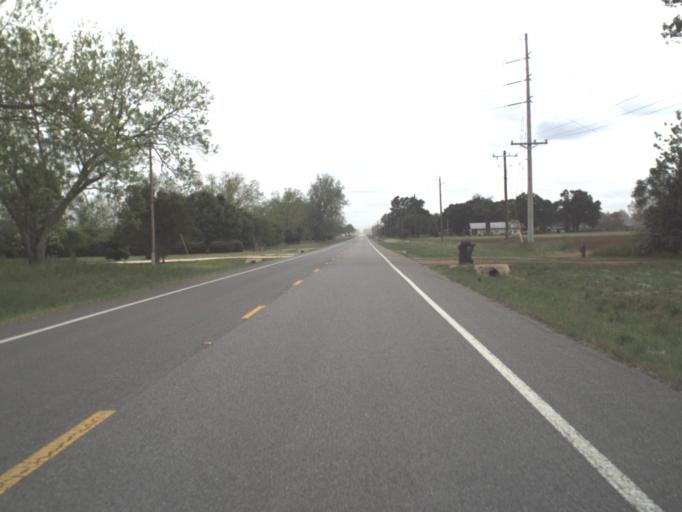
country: US
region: Florida
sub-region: Santa Rosa County
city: Point Baker
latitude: 30.7925
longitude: -87.0923
